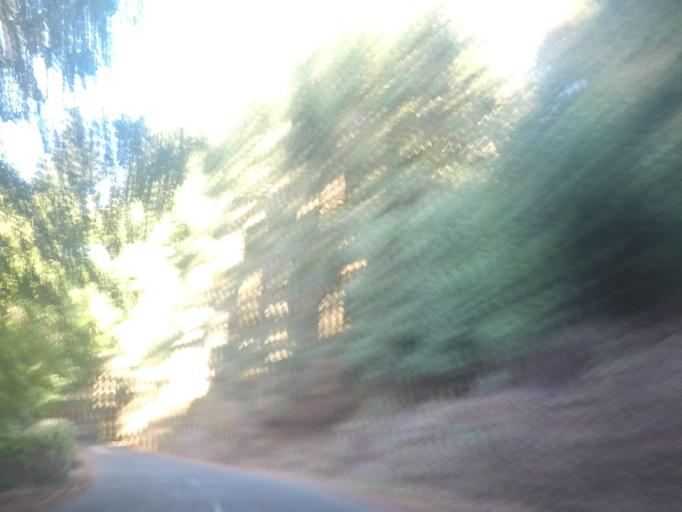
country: PT
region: Madeira
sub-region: Funchal
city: Nossa Senhora do Monte
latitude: 32.7090
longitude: -16.8899
